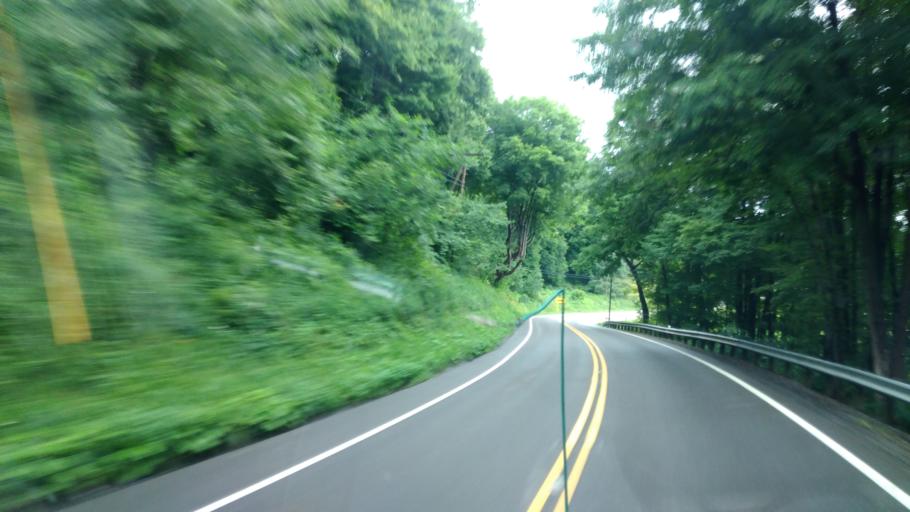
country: US
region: Ohio
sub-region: Stark County
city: Minerva
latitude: 40.6972
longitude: -81.0106
